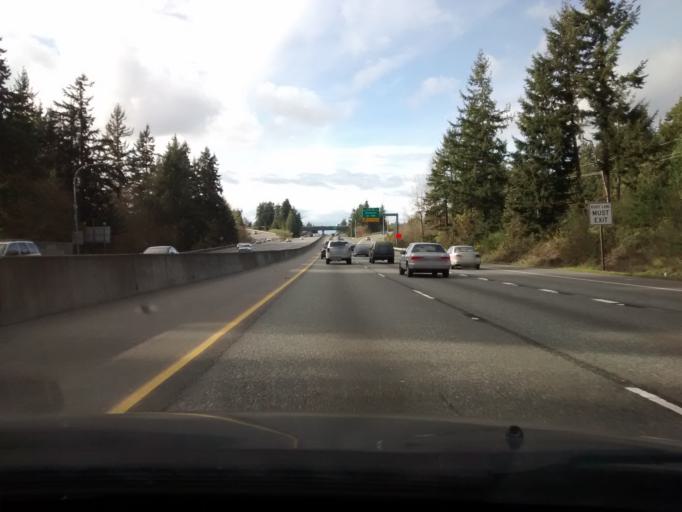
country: US
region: Washington
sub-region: Pierce County
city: Gig Harbor
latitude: 47.3009
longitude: -122.5724
